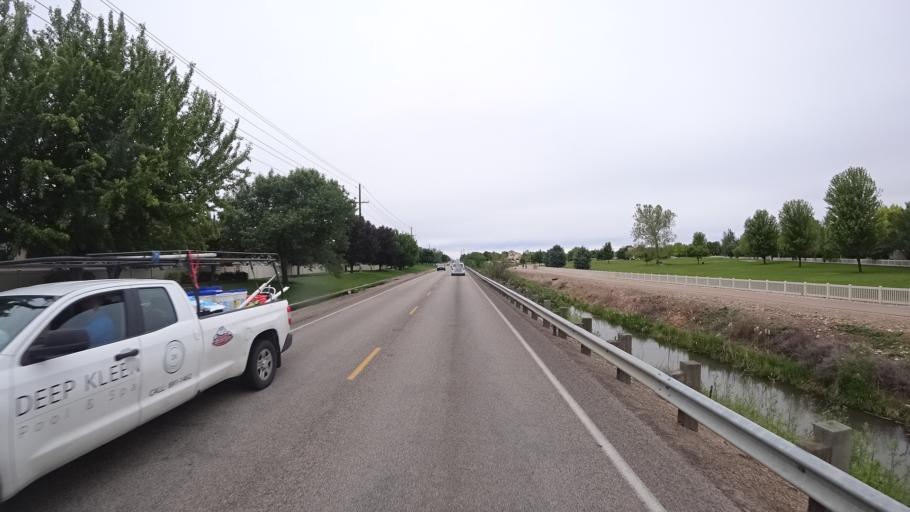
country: US
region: Idaho
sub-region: Ada County
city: Meridian
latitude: 43.6339
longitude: -116.4207
